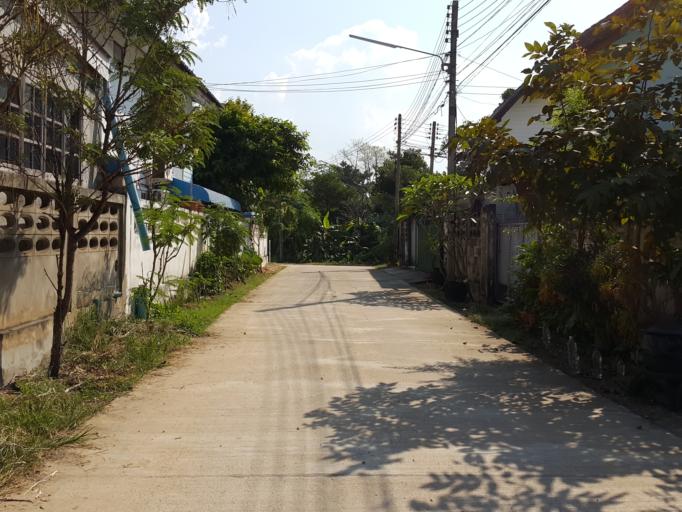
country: TH
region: Lampang
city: Lampang
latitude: 18.3047
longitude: 99.5023
